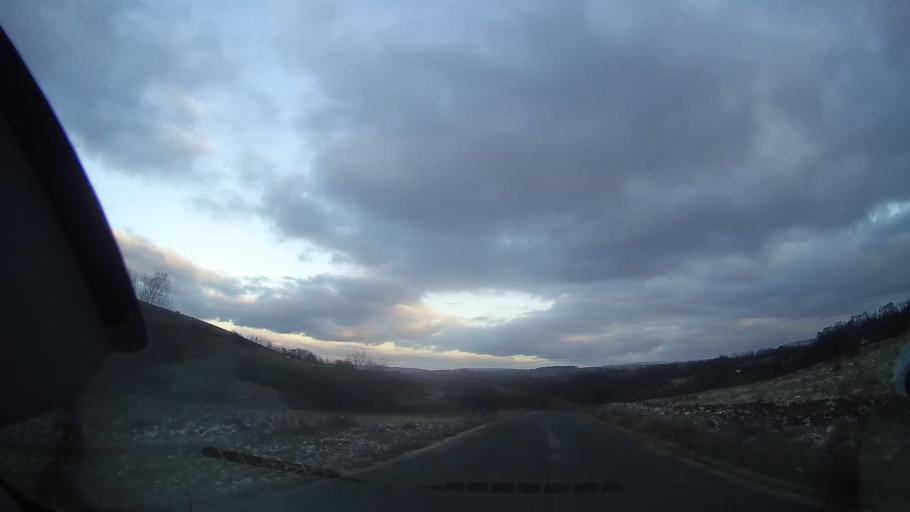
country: RO
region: Cluj
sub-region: Comuna Manastireni
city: Manastireni
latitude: 46.7811
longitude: 23.0675
